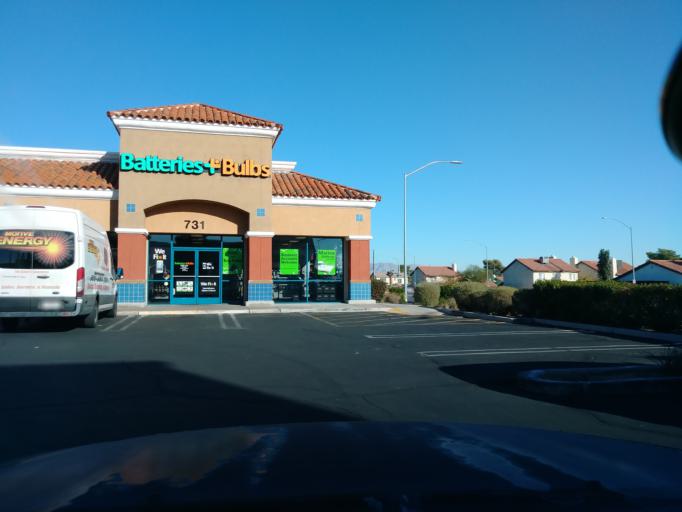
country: US
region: Nevada
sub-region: Clark County
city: Spring Valley
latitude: 36.1649
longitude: -115.2446
